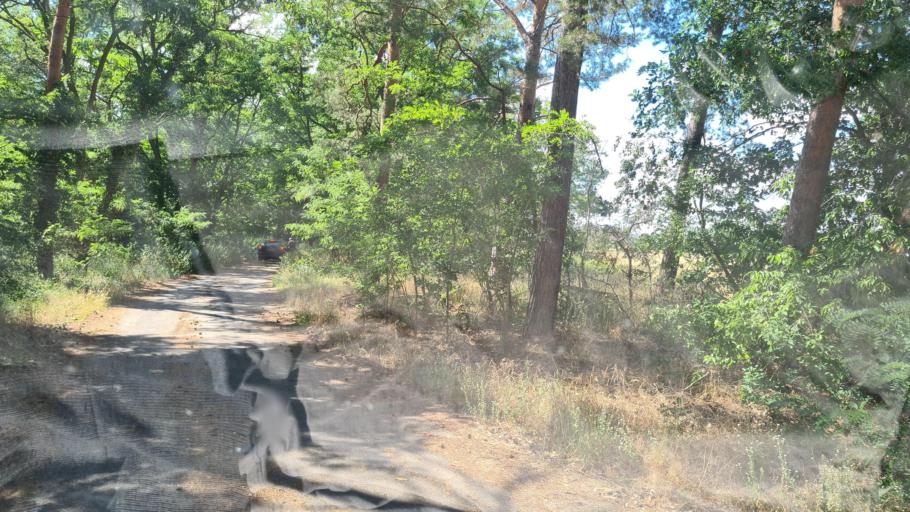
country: DE
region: Brandenburg
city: Trebbin
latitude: 52.1972
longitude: 13.2605
